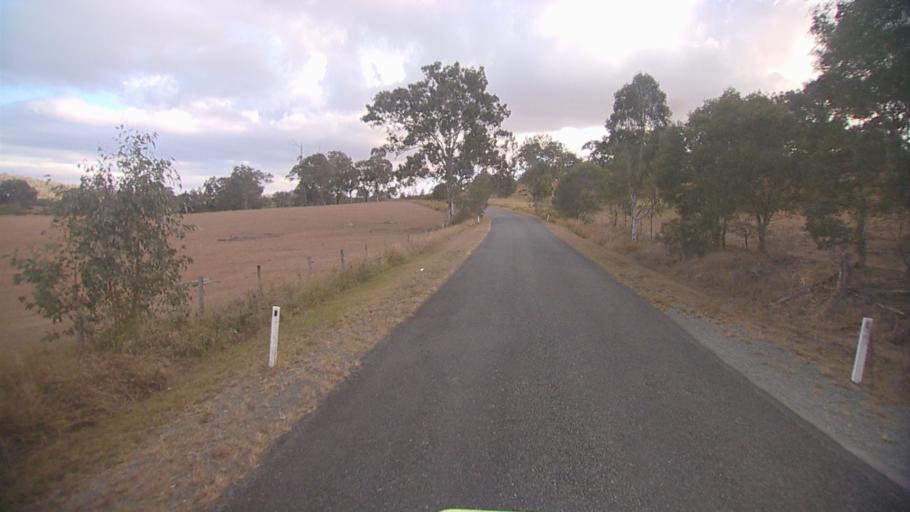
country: AU
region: Queensland
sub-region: Logan
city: Cedar Vale
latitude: -27.8903
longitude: 153.0672
